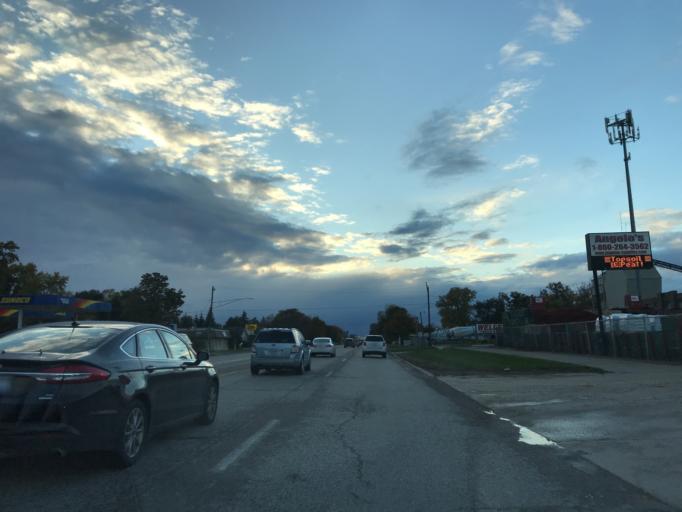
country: US
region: Michigan
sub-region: Oakland County
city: Farmington
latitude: 42.4416
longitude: -83.3402
